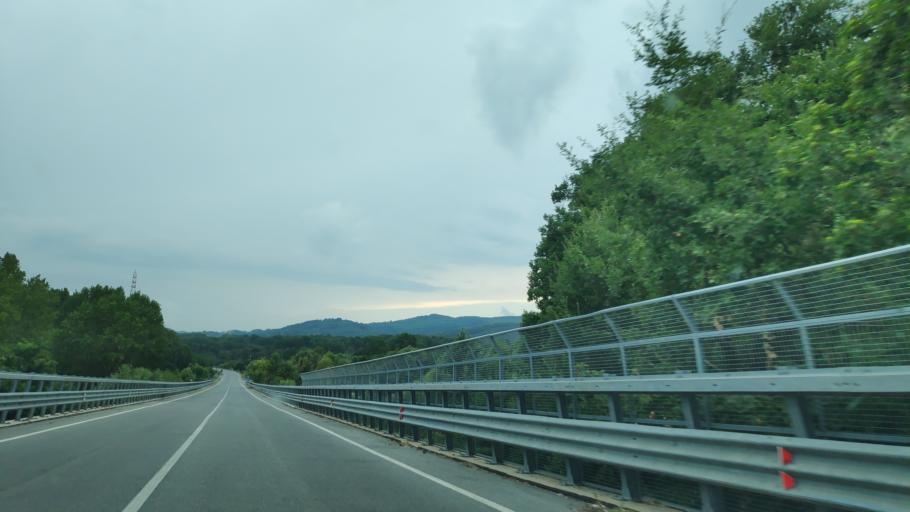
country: IT
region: Calabria
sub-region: Provincia di Catanzaro
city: Cardinale
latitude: 38.6652
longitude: 16.3949
